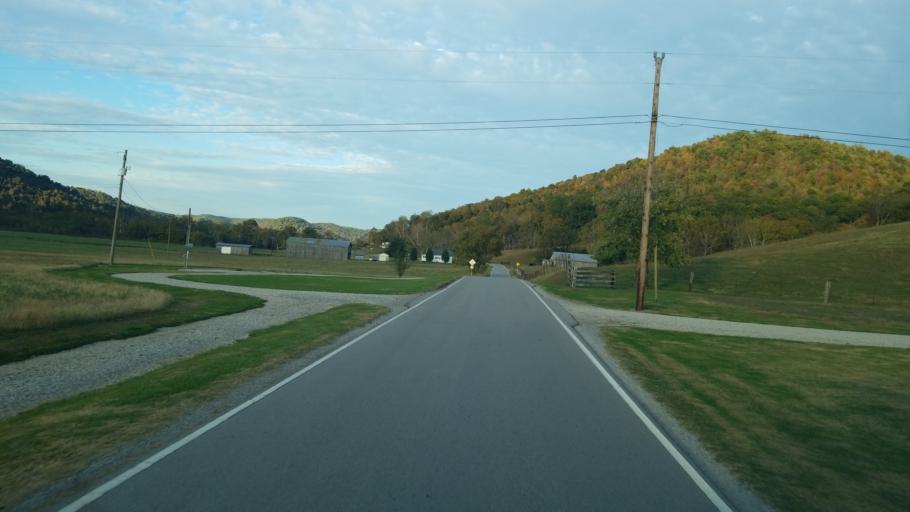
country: US
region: Kentucky
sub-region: Lewis County
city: Vanceburg
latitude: 38.5582
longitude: -83.4403
